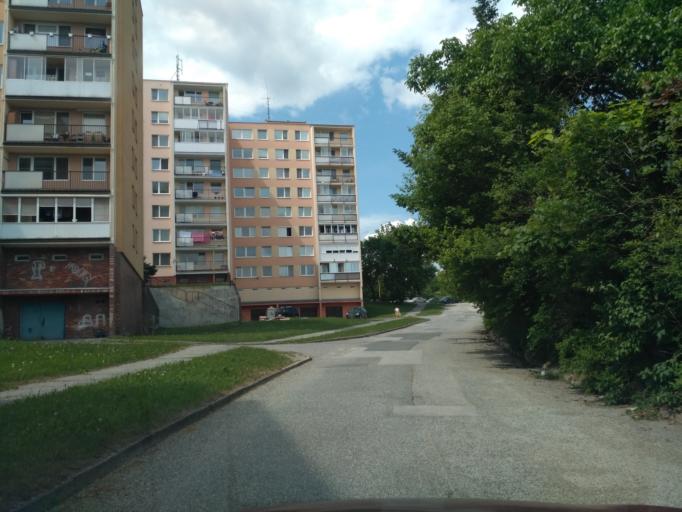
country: SK
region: Kosicky
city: Kosice
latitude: 48.7290
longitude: 21.2327
